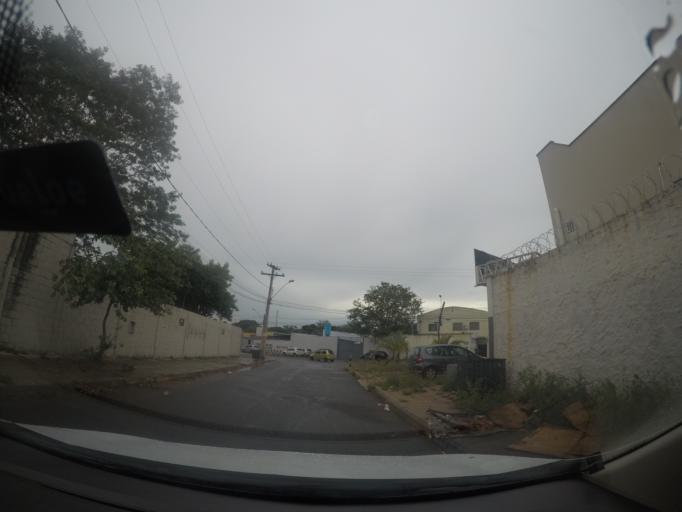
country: BR
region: Goias
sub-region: Goiania
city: Goiania
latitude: -16.6405
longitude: -49.2386
